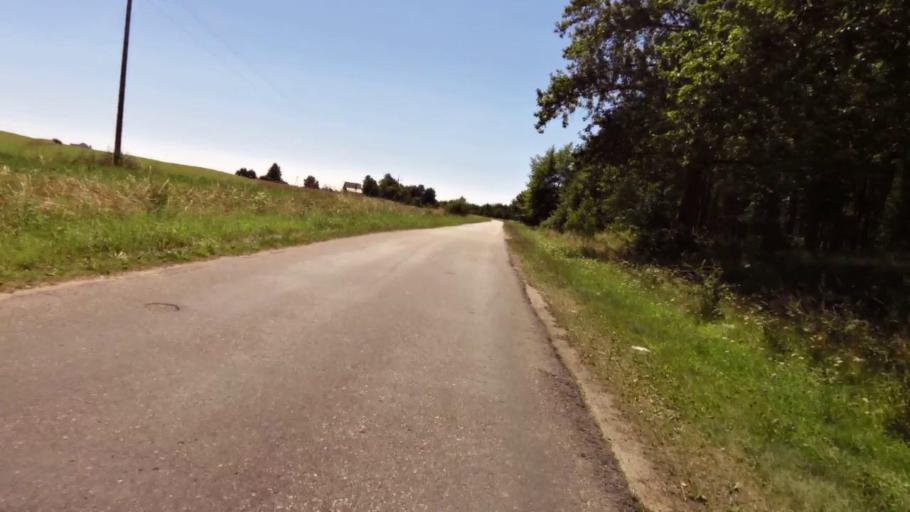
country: PL
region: West Pomeranian Voivodeship
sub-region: Powiat szczecinecki
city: Bialy Bor
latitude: 53.9330
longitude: 16.8533
